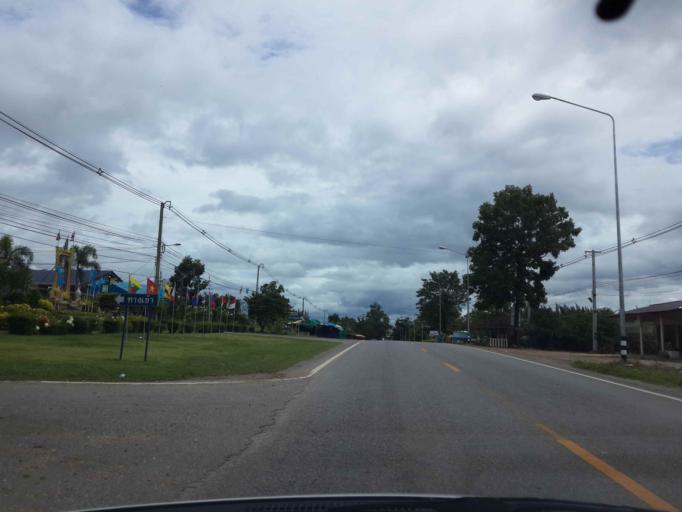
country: TH
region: Ratchaburi
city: Suan Phueng
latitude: 13.5445
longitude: 99.3180
